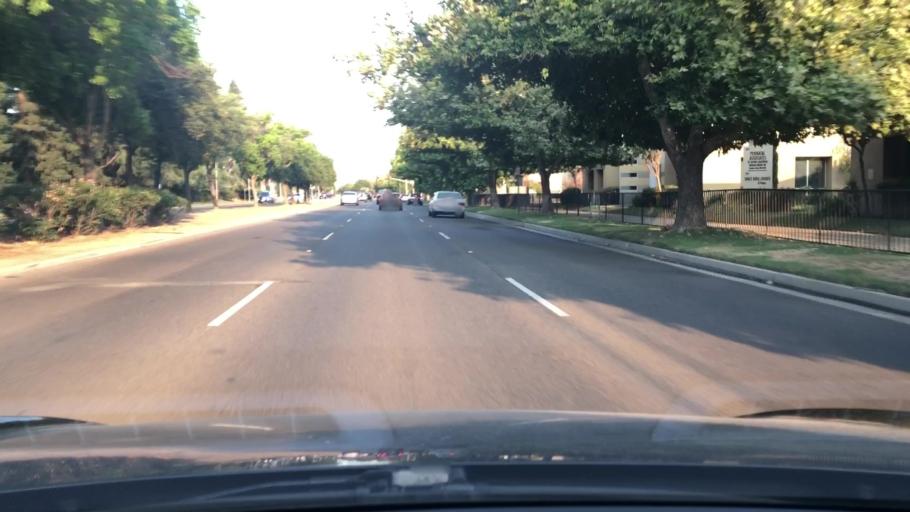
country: US
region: California
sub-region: Fresno County
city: Clovis
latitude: 36.8377
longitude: -119.7424
